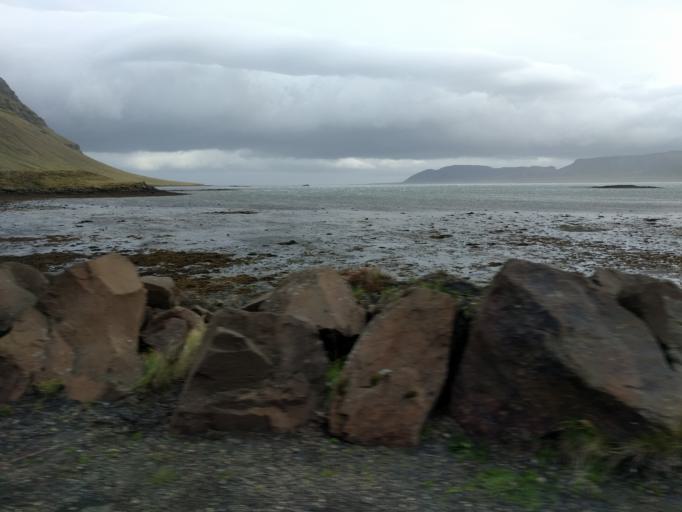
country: IS
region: West
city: Olafsvik
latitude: 64.9231
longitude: -23.2956
